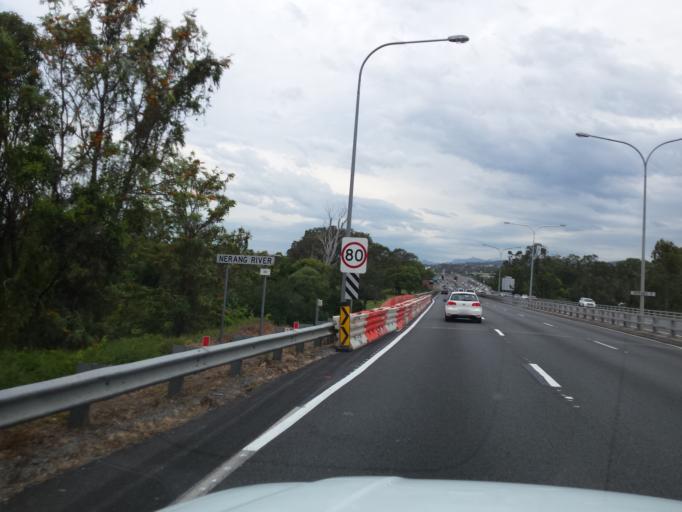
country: AU
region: Queensland
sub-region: Gold Coast
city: Nerang
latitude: -27.9858
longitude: 153.3414
